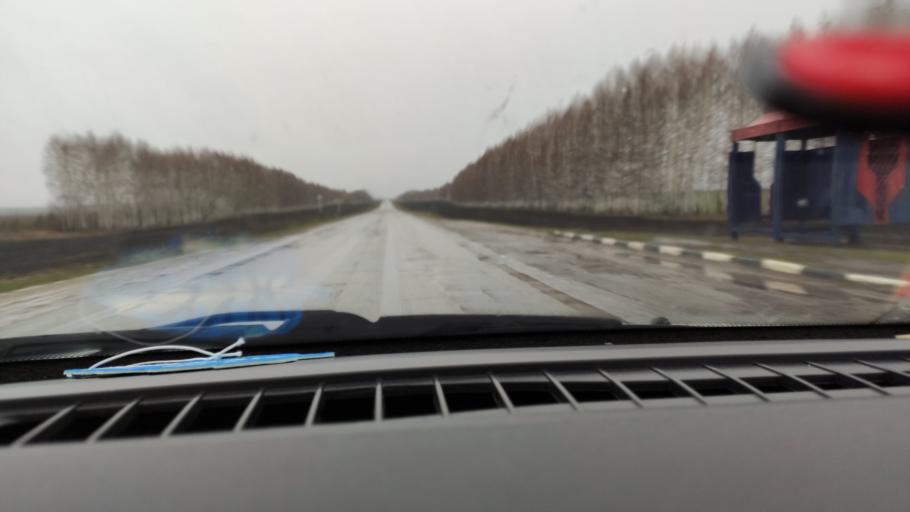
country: RU
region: Samara
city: Chelno-Vershiny
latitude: 54.6842
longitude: 51.0939
